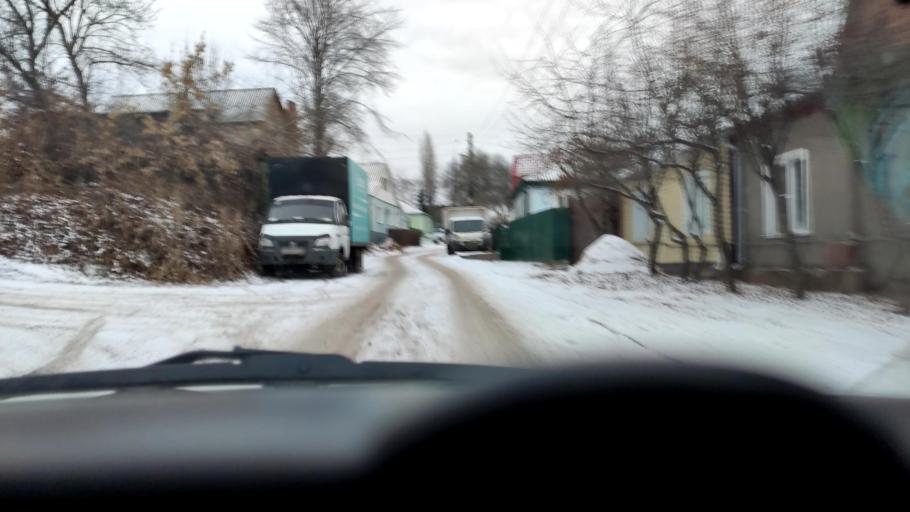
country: RU
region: Voronezj
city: Voronezh
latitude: 51.6332
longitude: 39.2048
